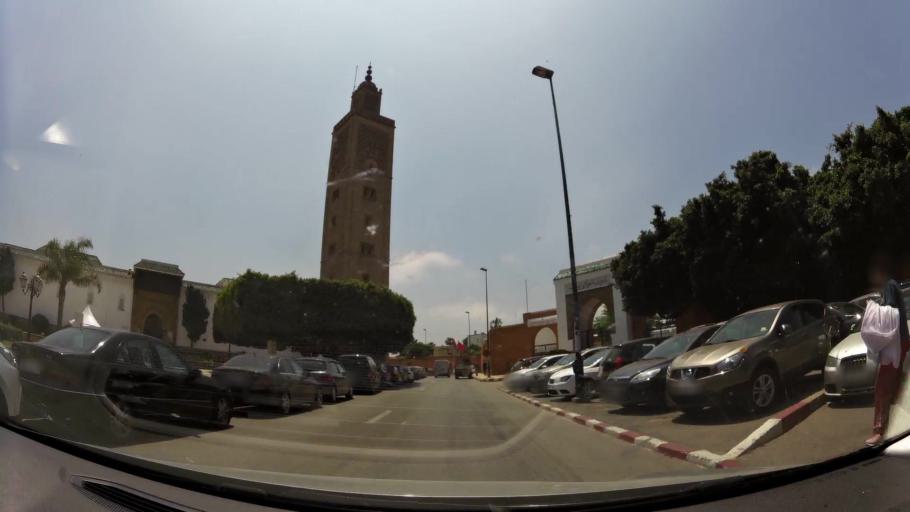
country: MA
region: Rabat-Sale-Zemmour-Zaer
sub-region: Rabat
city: Rabat
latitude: 34.0136
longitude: -6.8340
